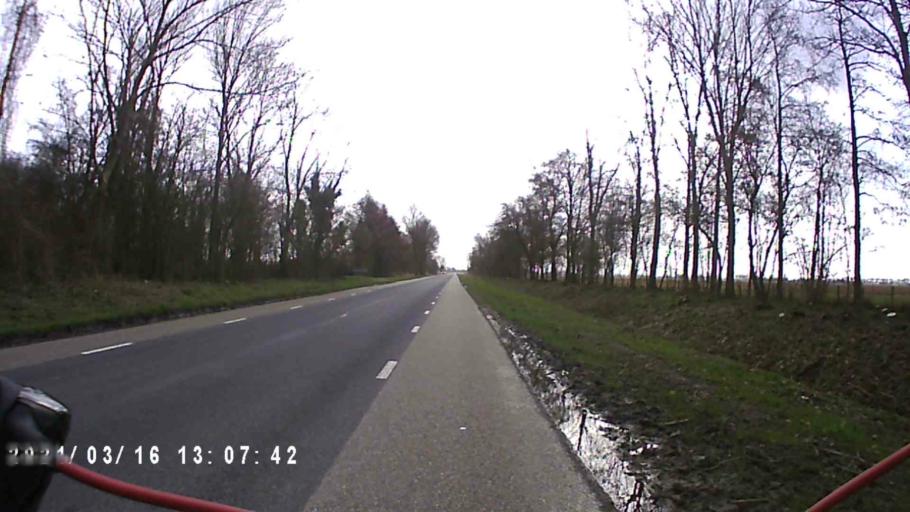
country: NL
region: Friesland
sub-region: Gemeente Het Bildt
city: Minnertsga
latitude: 53.2505
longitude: 5.6203
